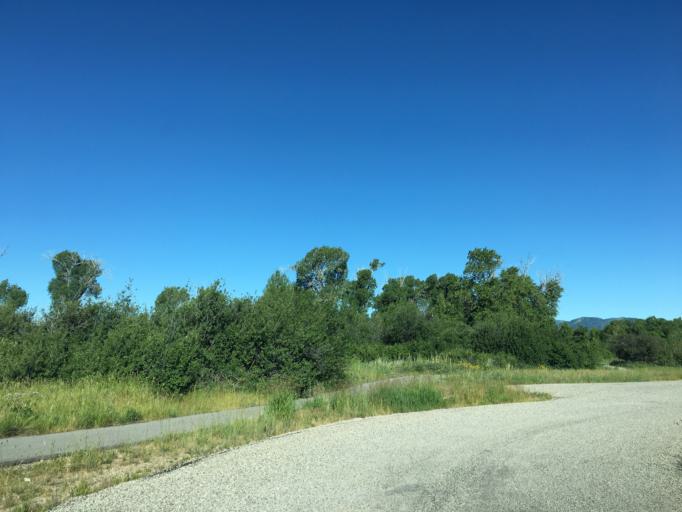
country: US
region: Idaho
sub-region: Teton County
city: Victor
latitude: 43.5897
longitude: -111.1016
